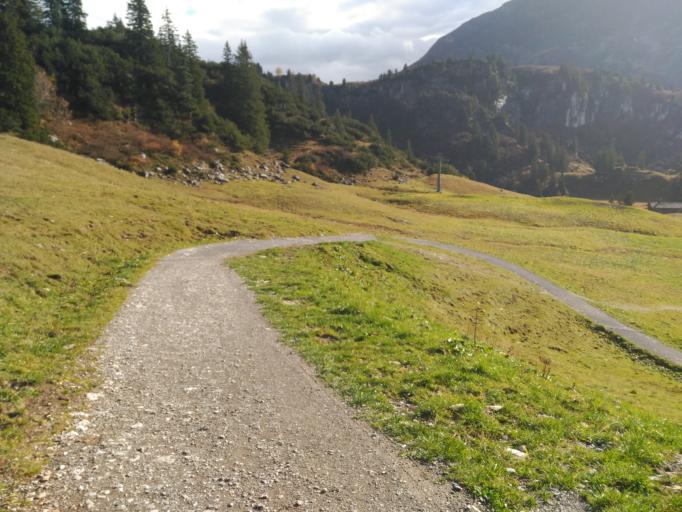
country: AT
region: Vorarlberg
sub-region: Politischer Bezirk Bregenz
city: Schroecken
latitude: 47.2577
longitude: 10.1117
